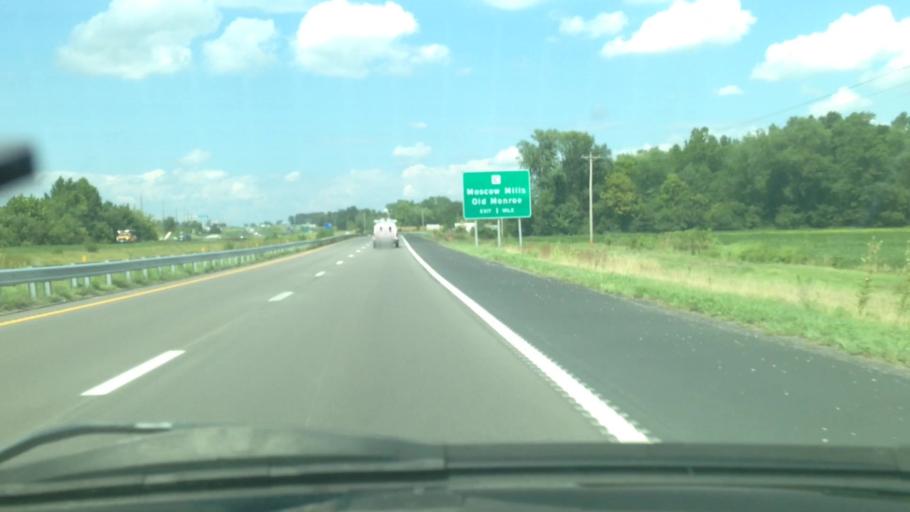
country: US
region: Missouri
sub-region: Lincoln County
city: Moscow Mills
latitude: 38.9252
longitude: -90.9249
